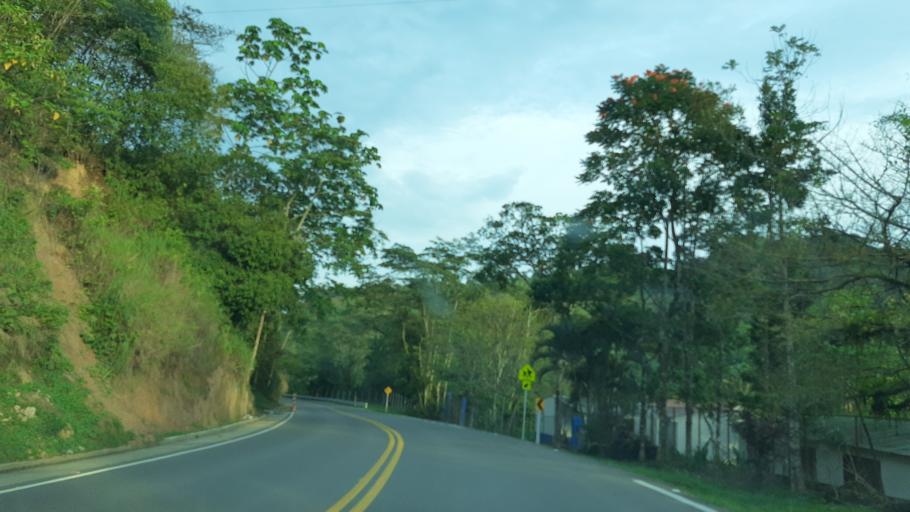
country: CO
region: Boyaca
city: San Luis de Gaceno
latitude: 4.8315
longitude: -73.1219
